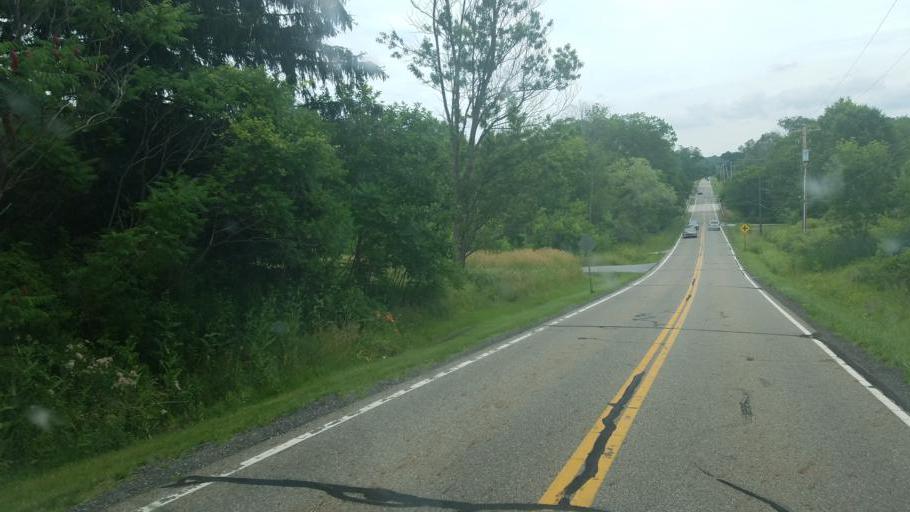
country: US
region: Ohio
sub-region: Geauga County
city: Burton
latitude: 41.4981
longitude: -81.1675
